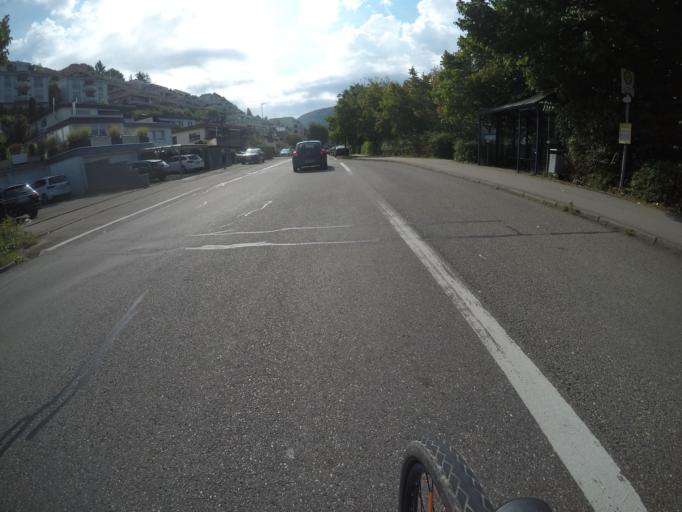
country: DE
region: Baden-Wuerttemberg
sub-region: Tuebingen Region
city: Bad Urach
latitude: 48.5051
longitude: 9.3773
